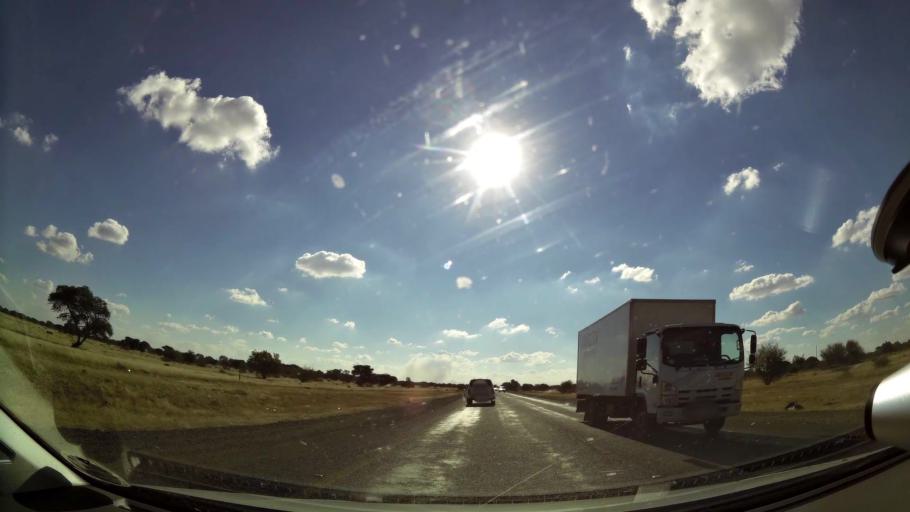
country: ZA
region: Northern Cape
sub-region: Frances Baard District Municipality
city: Kimberley
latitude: -28.7976
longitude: 24.7907
